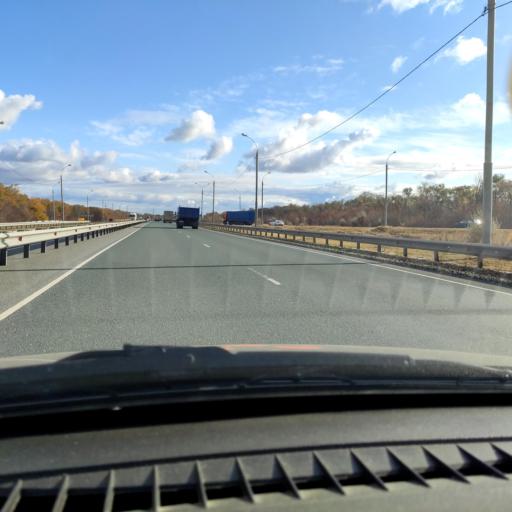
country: RU
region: Samara
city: Varlamovo
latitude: 53.1960
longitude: 48.2943
